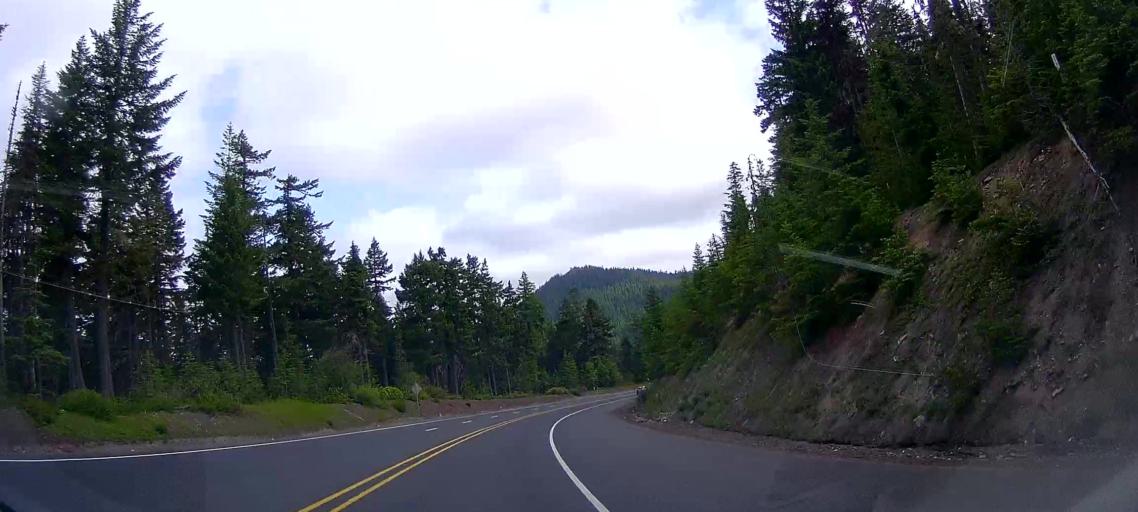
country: US
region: Oregon
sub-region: Clackamas County
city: Mount Hood Village
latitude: 45.2318
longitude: -121.7022
